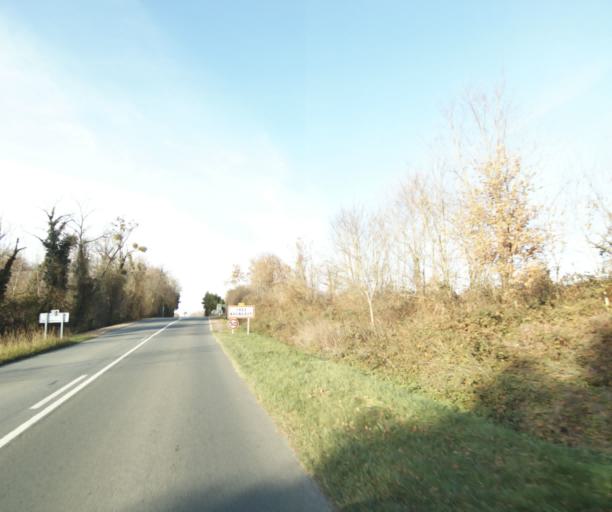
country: FR
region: Poitou-Charentes
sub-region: Departement de la Charente-Maritime
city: Burie
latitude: 45.7998
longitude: -0.4447
